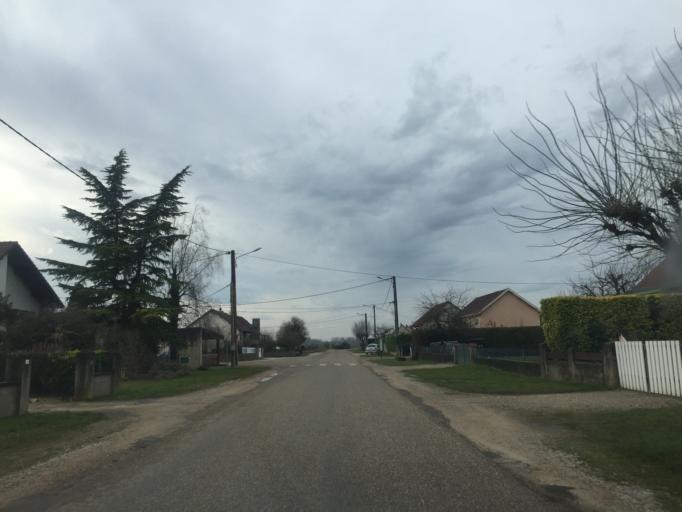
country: FR
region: Franche-Comte
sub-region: Departement du Jura
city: Tavaux
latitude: 47.0368
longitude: 5.4370
